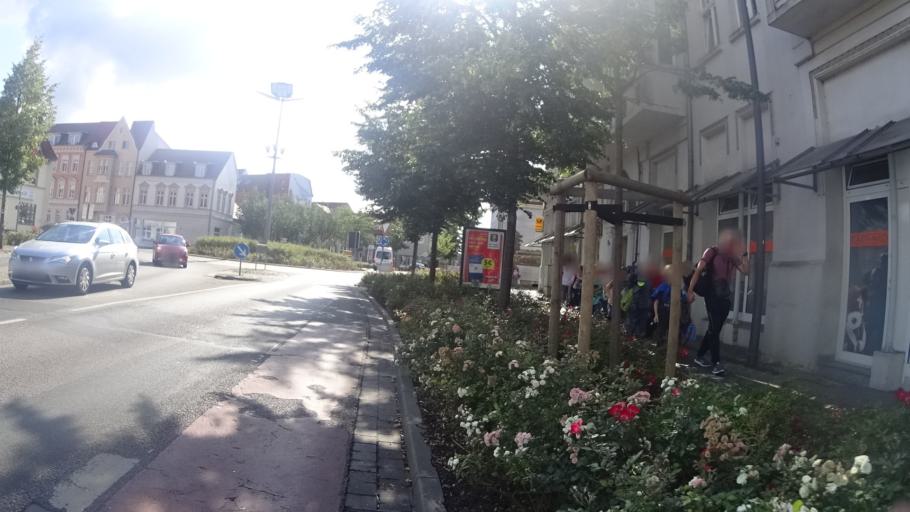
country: DE
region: Brandenburg
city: Wittenberge
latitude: 52.9951
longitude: 11.7519
